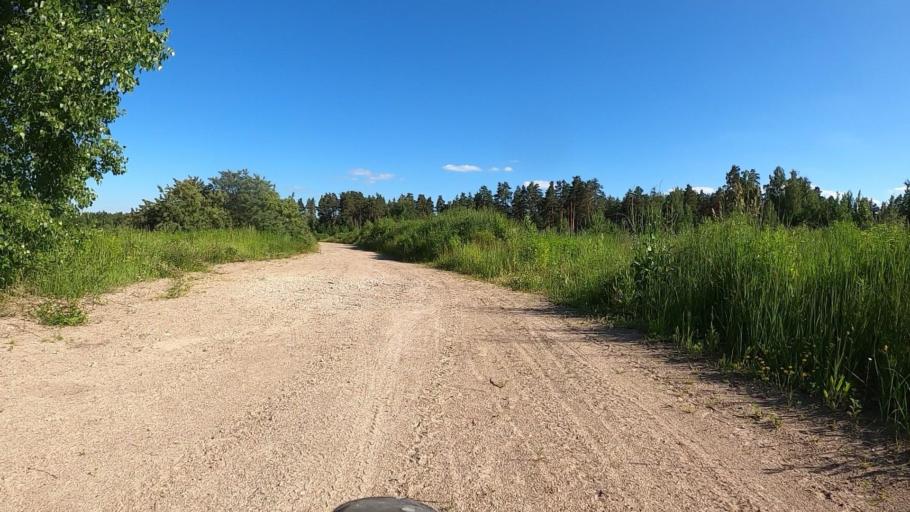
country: LV
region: Stopini
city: Ulbroka
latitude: 56.8778
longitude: 24.2769
